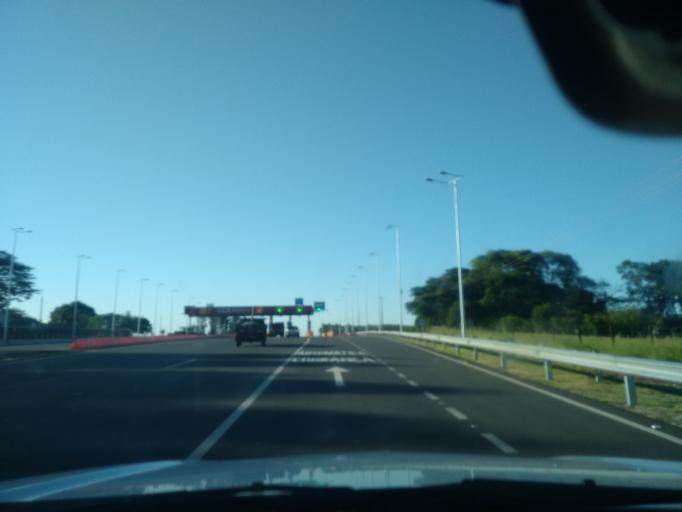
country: BR
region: Mato Grosso do Sul
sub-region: Eldorado
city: Eldorado
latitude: -23.8661
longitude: -54.3291
